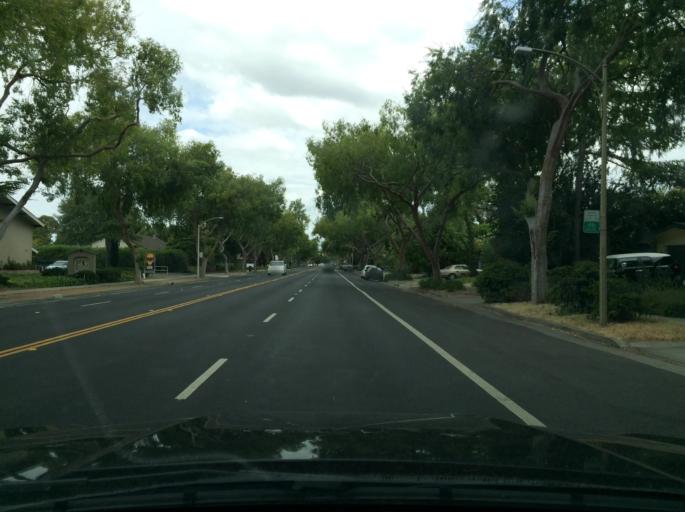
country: US
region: California
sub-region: Santa Clara County
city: Palo Alto
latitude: 37.4260
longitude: -122.1176
